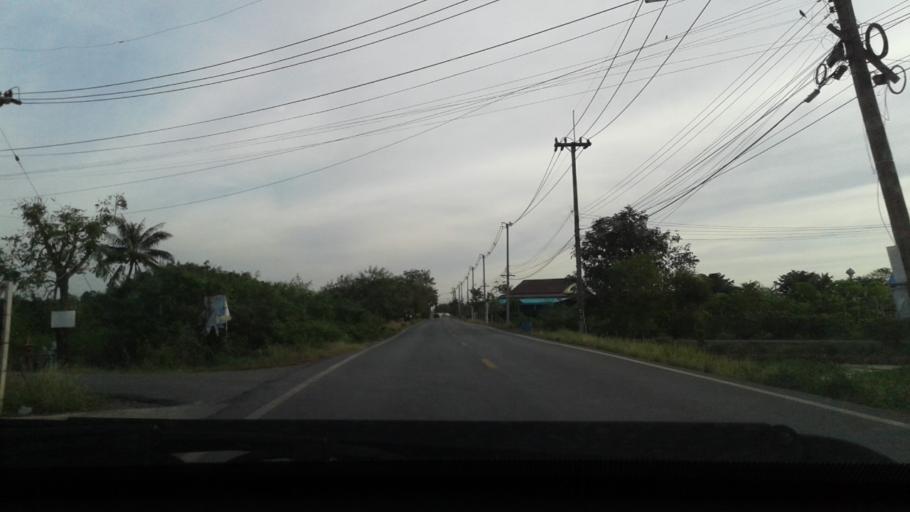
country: TH
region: Nonthaburi
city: Sai Noi
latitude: 13.9176
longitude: 100.2553
